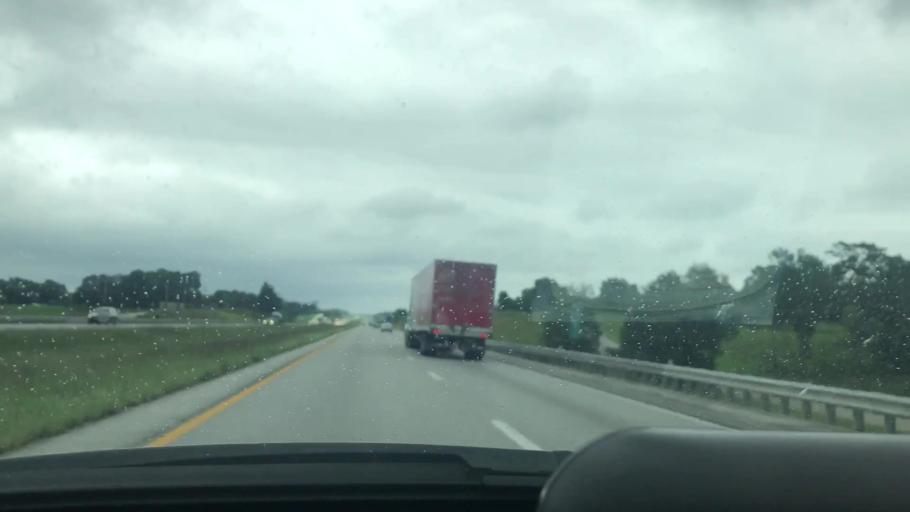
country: US
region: Missouri
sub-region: Jasper County
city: Duenweg
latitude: 37.0827
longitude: -94.3341
